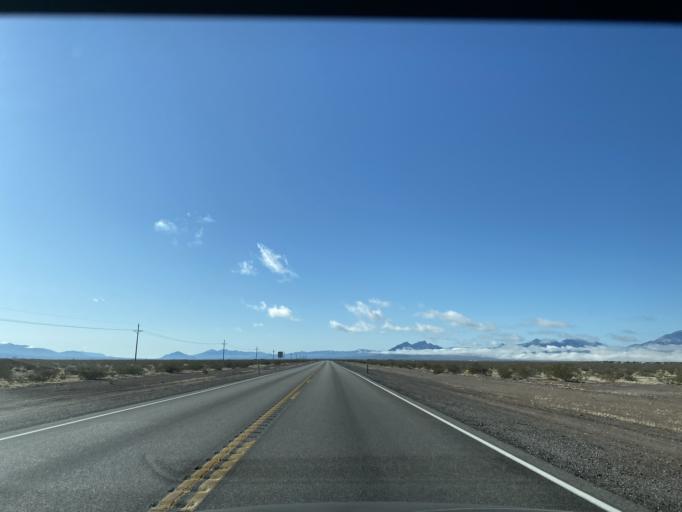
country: US
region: Nevada
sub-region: Nye County
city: Beatty
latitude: 36.5660
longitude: -116.4142
